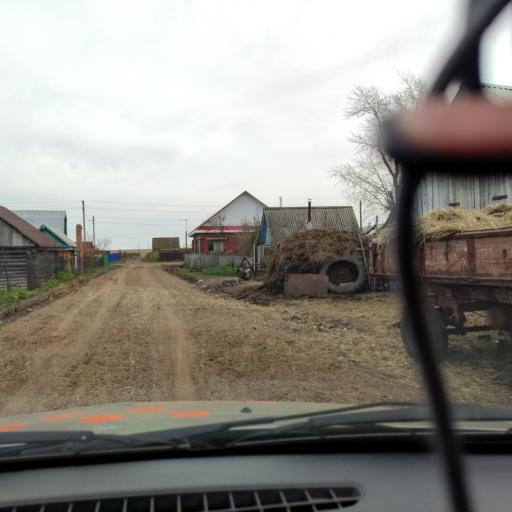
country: RU
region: Bashkortostan
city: Kabakovo
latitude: 54.5289
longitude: 56.0264
